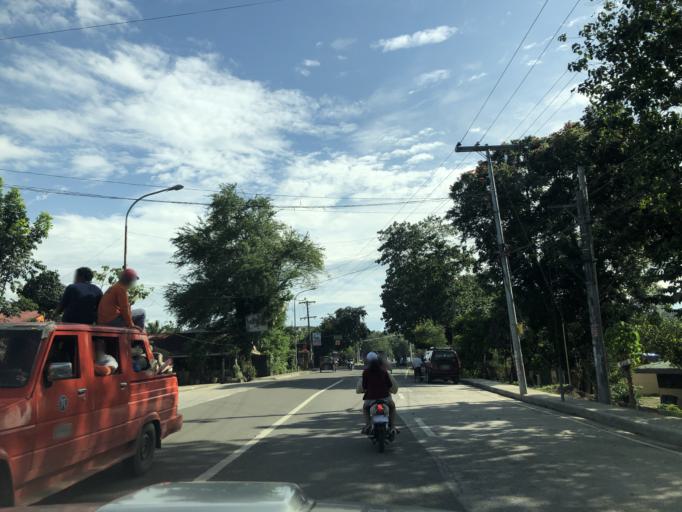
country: PH
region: Western Visayas
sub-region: Province of Iloilo
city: Maribong
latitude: 11.1214
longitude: 122.5388
